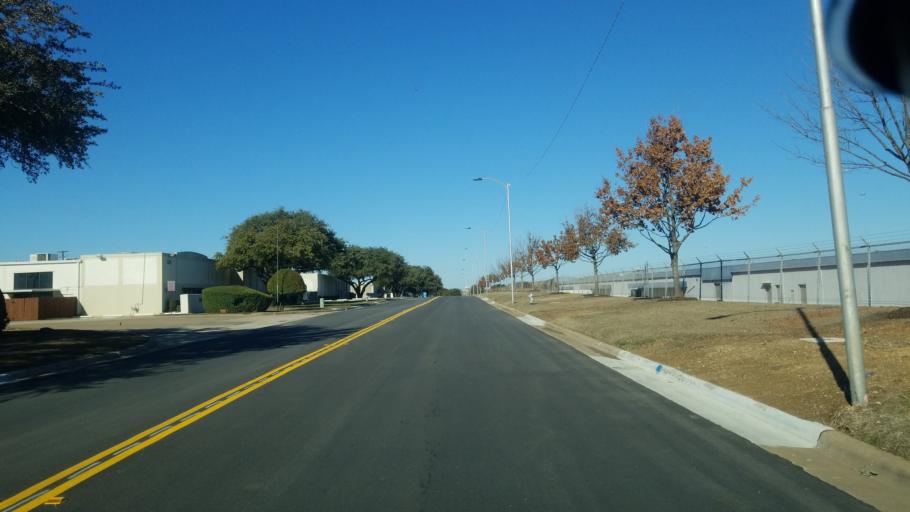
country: US
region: Texas
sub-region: Tarrant County
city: Arlington
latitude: 32.7510
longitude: -97.0542
